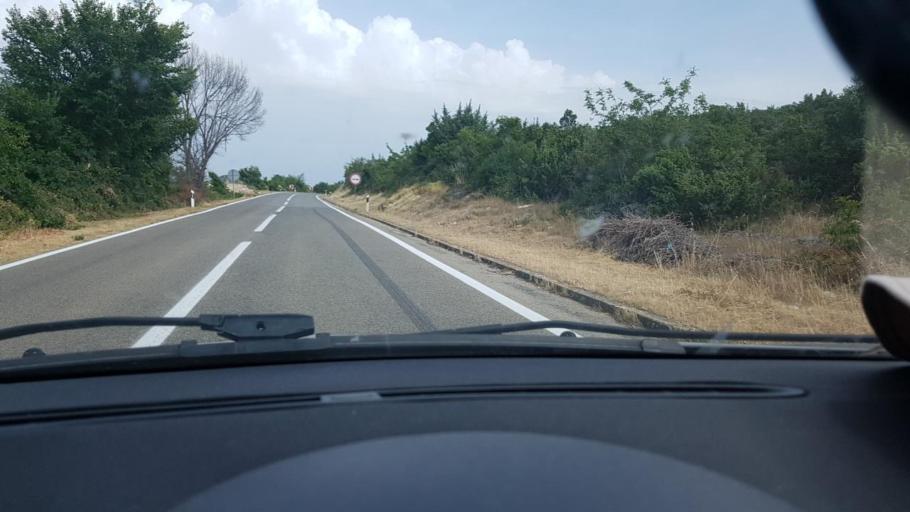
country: HR
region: Sibensko-Kniniska
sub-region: Grad Sibenik
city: Pirovac
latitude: 43.8659
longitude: 15.7406
